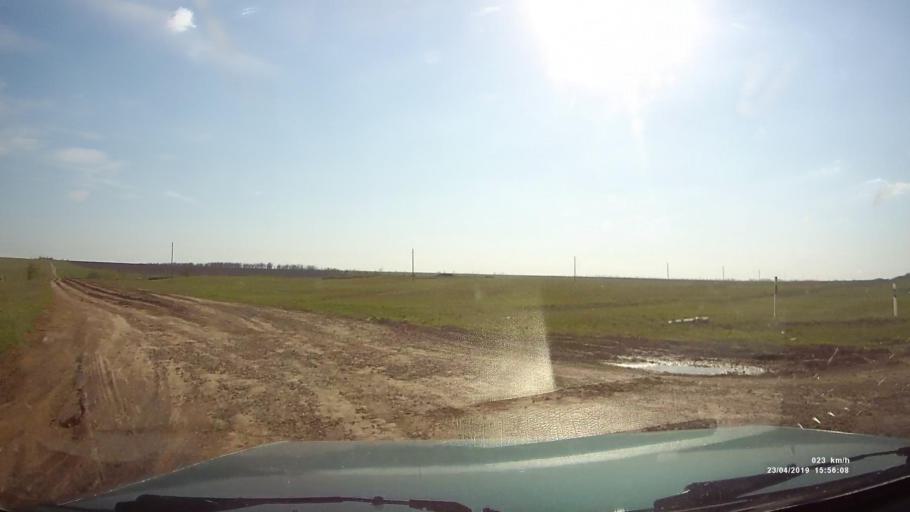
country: RU
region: Rostov
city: Remontnoye
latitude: 46.5384
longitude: 43.1115
